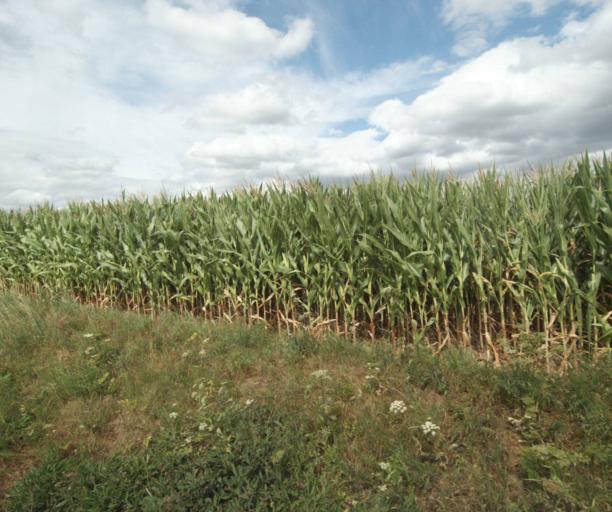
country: FR
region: Nord-Pas-de-Calais
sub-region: Departement du Nord
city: Roncq
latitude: 50.7642
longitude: 3.1046
